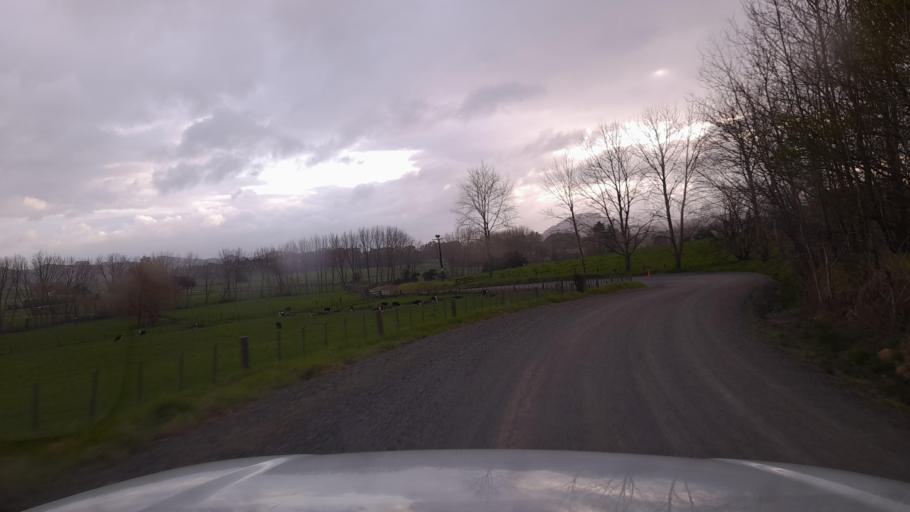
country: NZ
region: Northland
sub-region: Whangarei
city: Maungatapere
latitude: -35.6317
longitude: 174.1938
